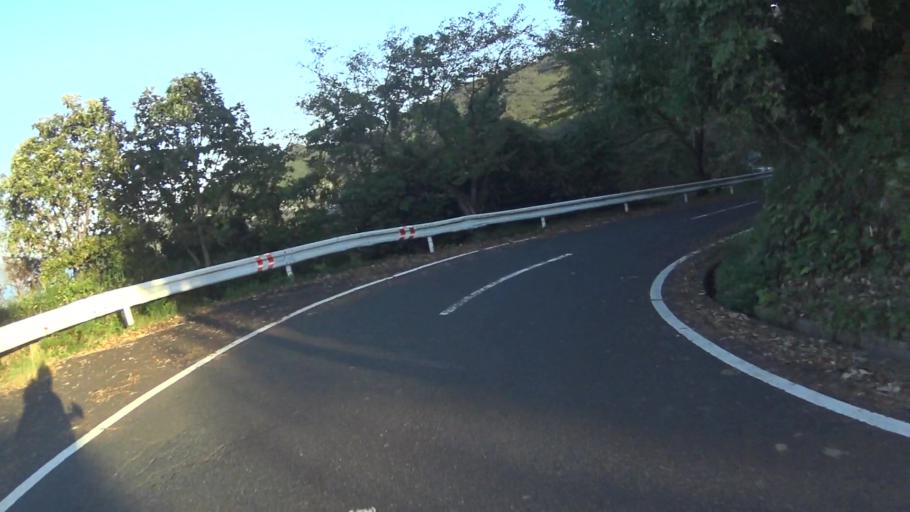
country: JP
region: Hyogo
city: Toyooka
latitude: 35.6919
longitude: 134.9871
